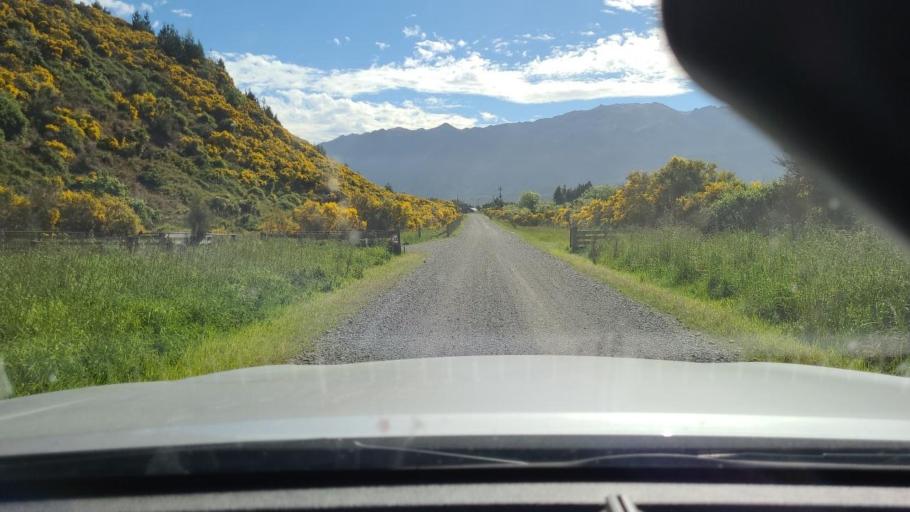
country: NZ
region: Southland
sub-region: Southland District
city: Te Anau
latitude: -45.6949
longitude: 167.6435
